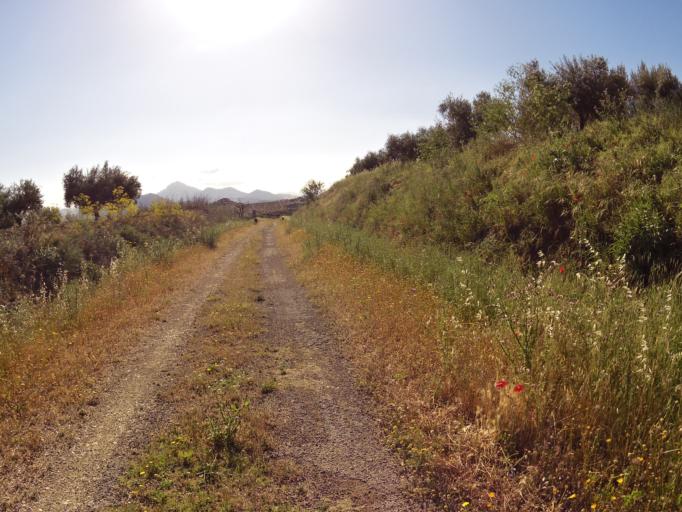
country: ES
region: Andalusia
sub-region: Province of Cordoba
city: Fuente-Tojar
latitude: 37.5831
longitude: -4.1902
